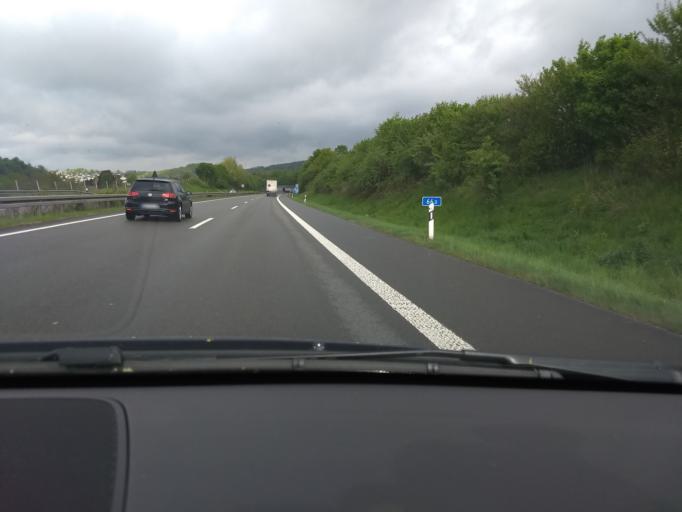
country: DE
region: North Rhine-Westphalia
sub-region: Regierungsbezirk Arnsberg
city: Arnsberg
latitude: 51.3978
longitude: 8.0948
